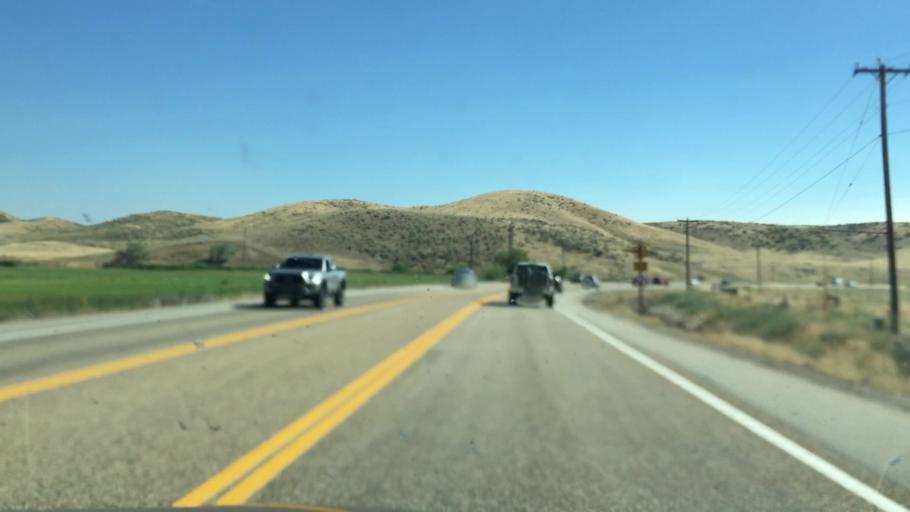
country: US
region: Idaho
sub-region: Ada County
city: Eagle
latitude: 43.7320
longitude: -116.3042
